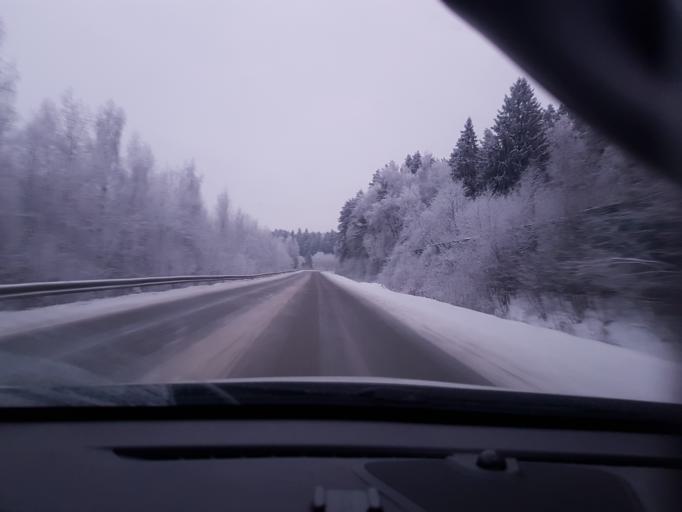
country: RU
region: Moskovskaya
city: Snegiri
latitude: 55.8459
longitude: 36.9590
